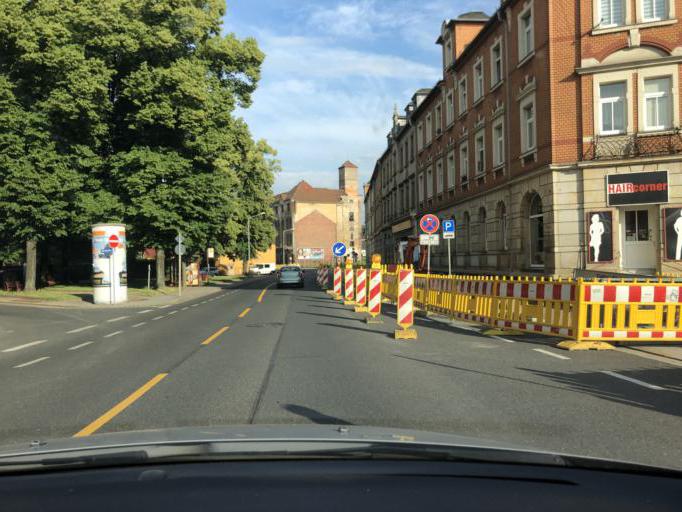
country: DE
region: Saxony
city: Freital
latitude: 50.9969
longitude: 13.6499
